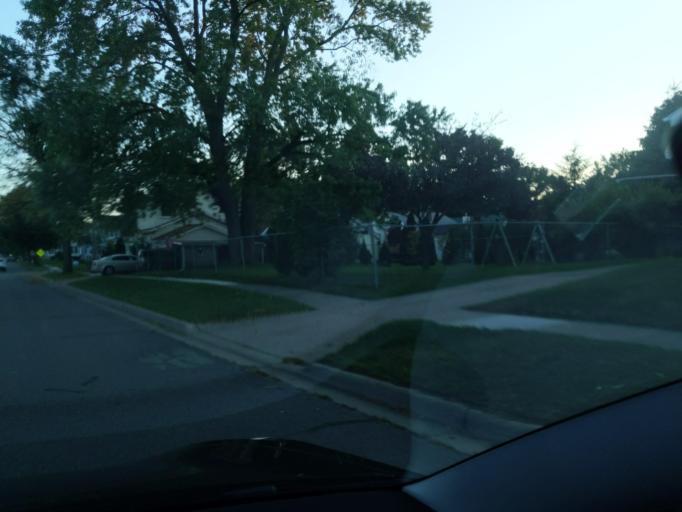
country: US
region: Michigan
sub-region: Jackson County
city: Jackson
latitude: 42.2646
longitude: -84.3844
